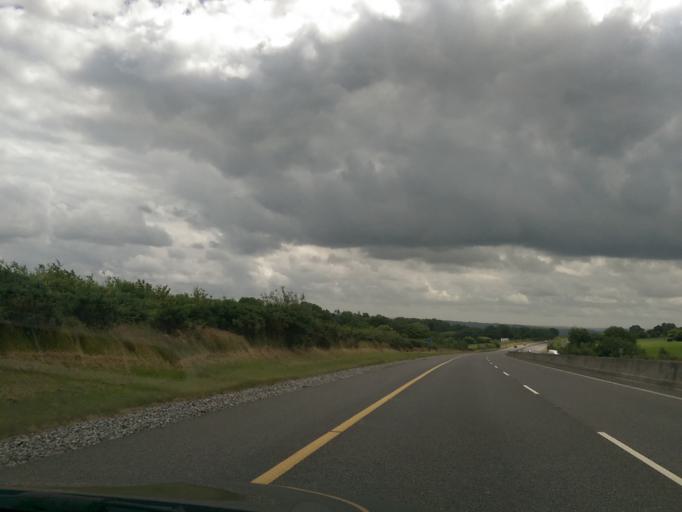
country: IE
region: Munster
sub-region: County Cork
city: Mitchelstown
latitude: 52.2091
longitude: -8.2754
